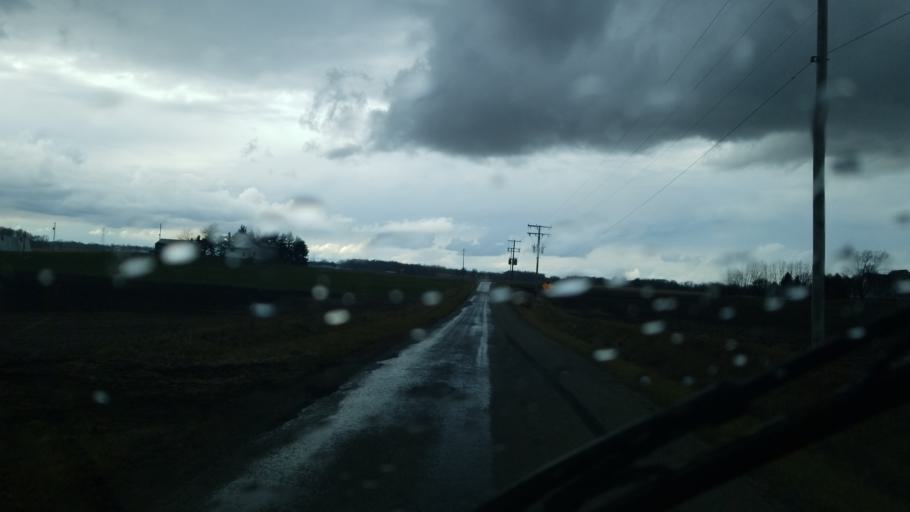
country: US
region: Ohio
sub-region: Crawford County
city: Bucyrus
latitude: 40.8577
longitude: -82.8527
